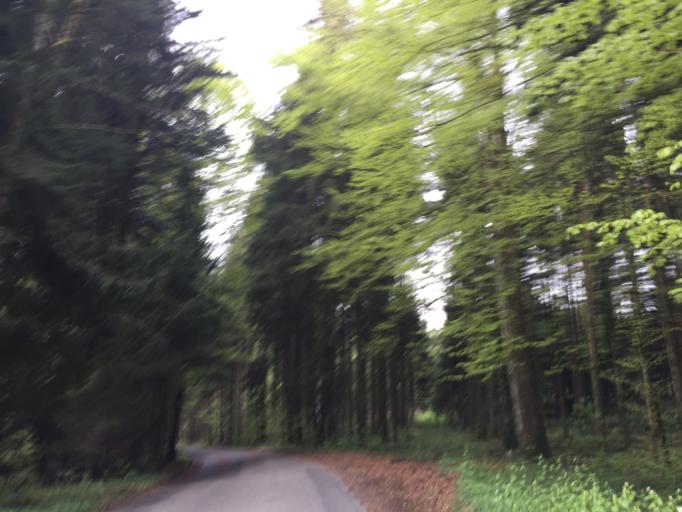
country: CH
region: Bern
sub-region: Bern-Mittelland District
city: Rubigen
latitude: 46.9241
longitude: 7.5369
